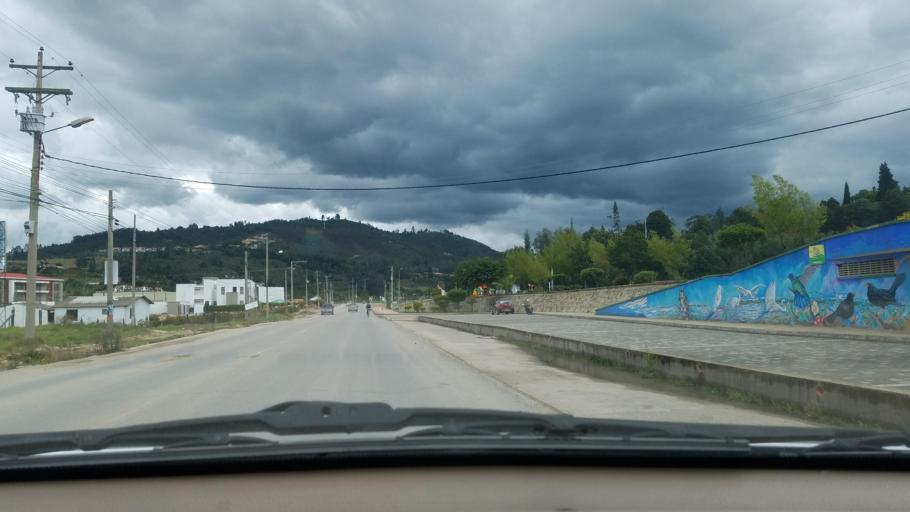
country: CO
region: Boyaca
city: Paipa
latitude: 5.7661
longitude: -73.1118
